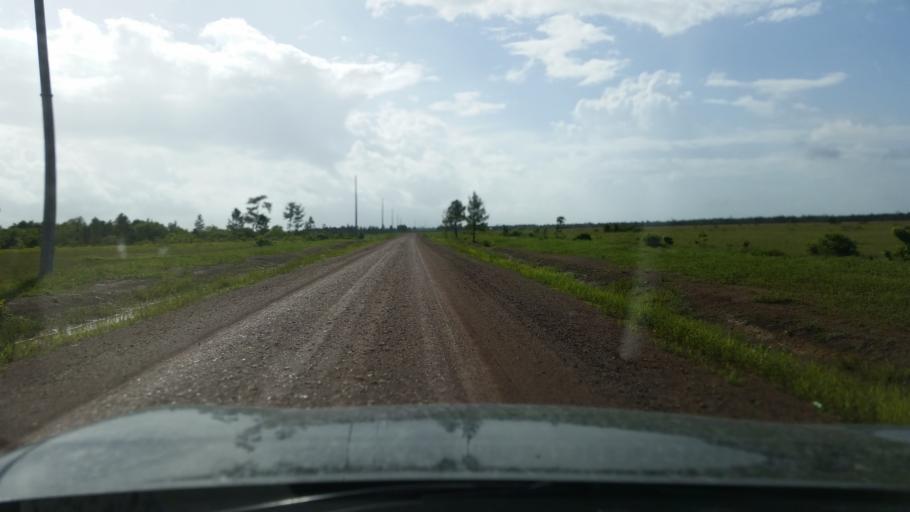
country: NI
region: Atlantico Norte (RAAN)
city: Puerto Cabezas
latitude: 14.1088
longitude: -83.5768
